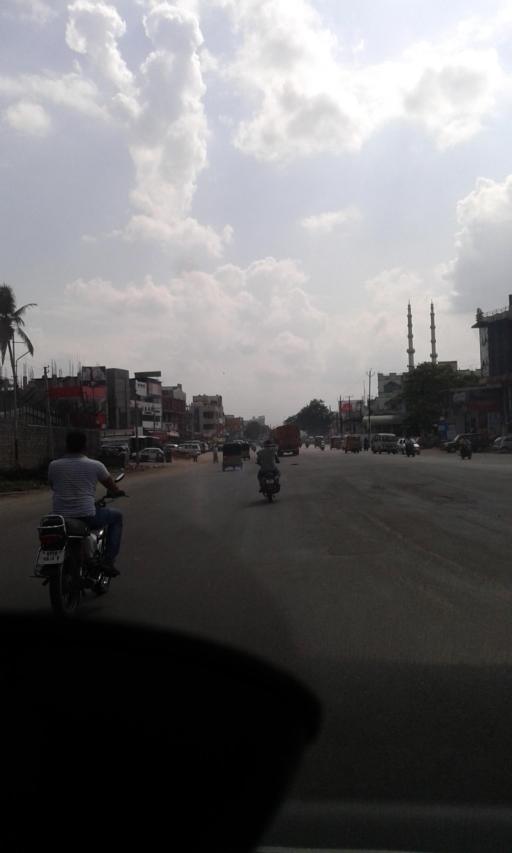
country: IN
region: Telangana
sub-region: Rangareddi
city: Balapur
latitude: 17.3289
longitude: 78.4827
